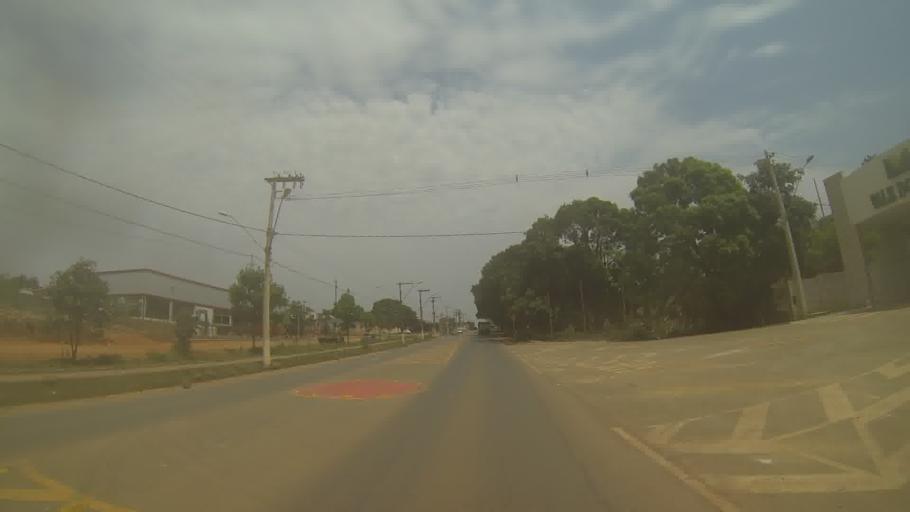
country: BR
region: Minas Gerais
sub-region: Bambui
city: Bambui
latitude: -20.0158
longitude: -45.9644
